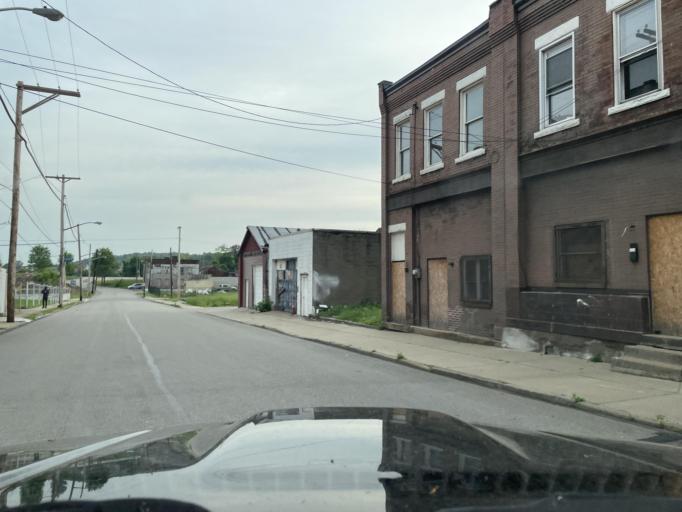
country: US
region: Pennsylvania
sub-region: Allegheny County
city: Wilkinsburg
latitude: 40.4512
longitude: -79.8901
